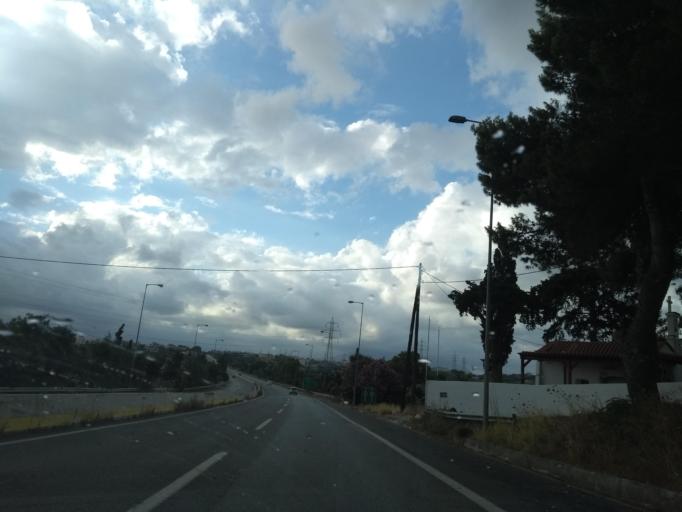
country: GR
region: Crete
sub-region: Nomos Irakleiou
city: Gazi
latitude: 35.3250
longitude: 25.0570
